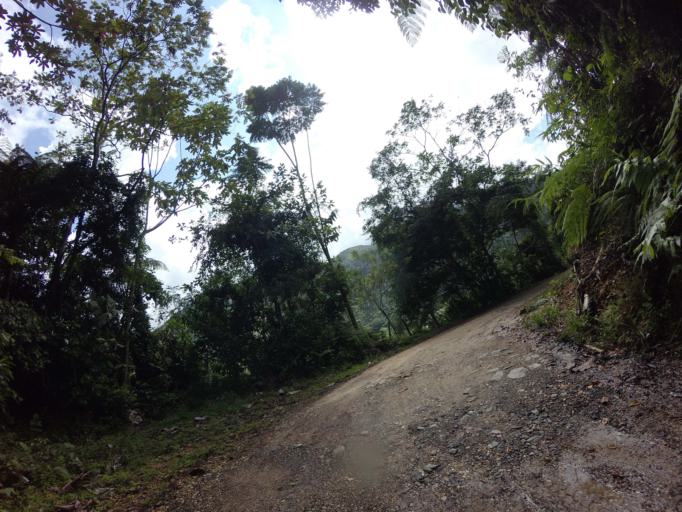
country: CO
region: Antioquia
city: Narino
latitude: 5.5375
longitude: -75.1347
